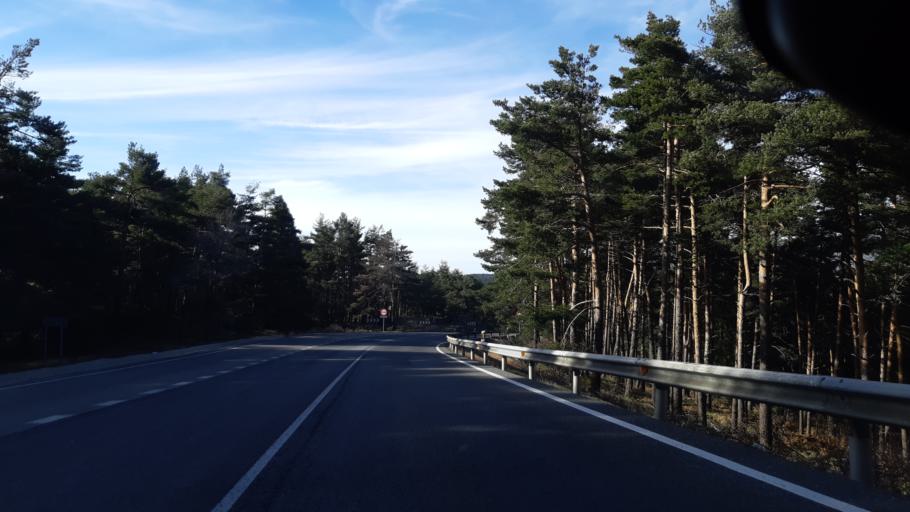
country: ES
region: Madrid
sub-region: Provincia de Madrid
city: Guadarrama
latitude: 40.7057
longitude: -4.1483
